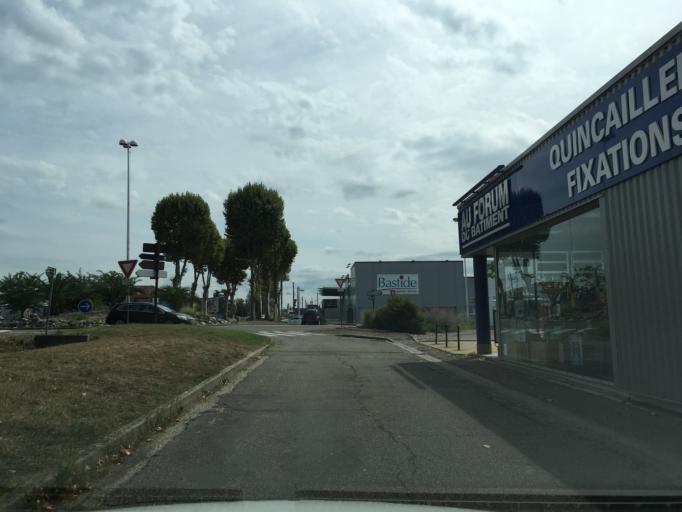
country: FR
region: Aquitaine
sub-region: Departement du Lot-et-Garonne
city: Agen
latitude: 44.1837
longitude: 0.6219
